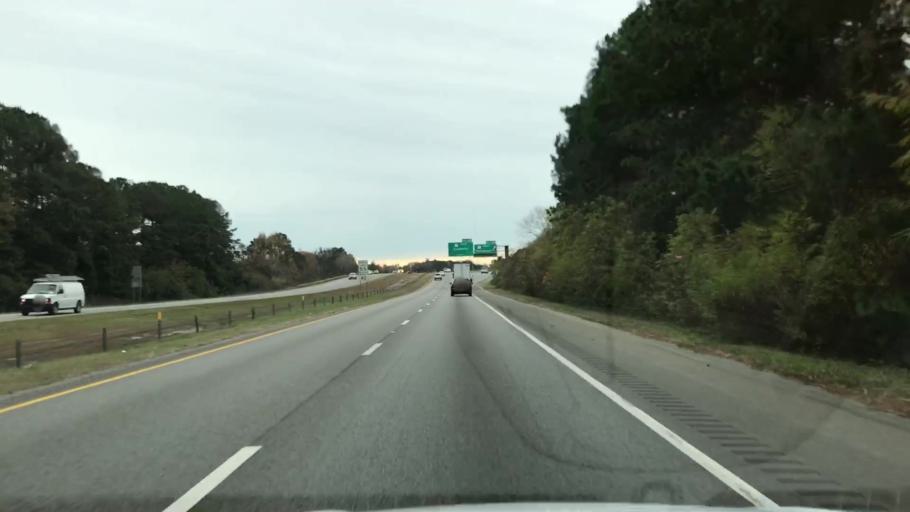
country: US
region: South Carolina
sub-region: Charleston County
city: Mount Pleasant
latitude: 32.8273
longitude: -79.8512
